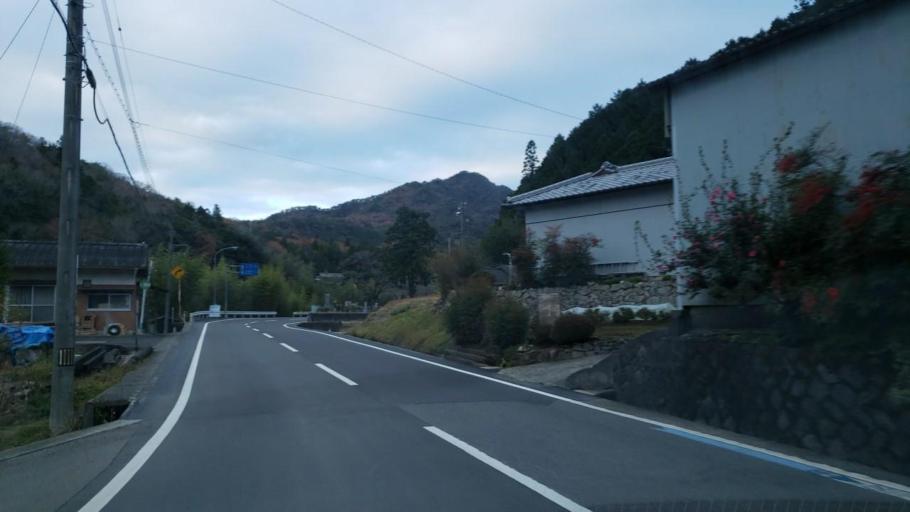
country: JP
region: Tokushima
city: Wakimachi
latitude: 34.1761
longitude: 134.1909
